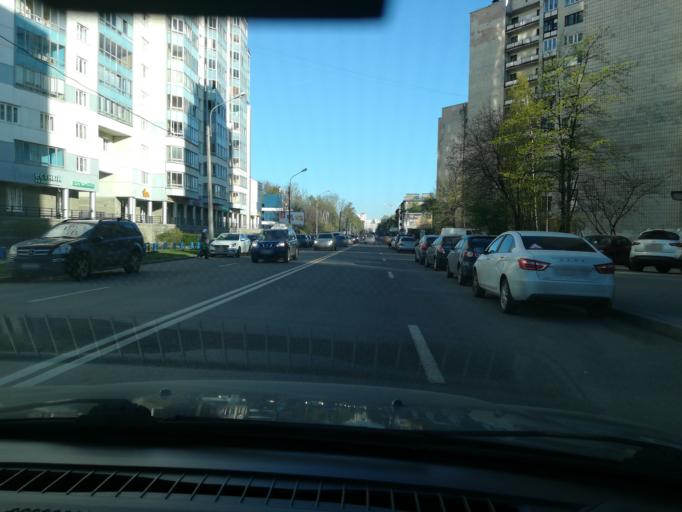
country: RU
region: St.-Petersburg
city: Vasyl'evsky Ostrov
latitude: 59.9459
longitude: 30.2359
